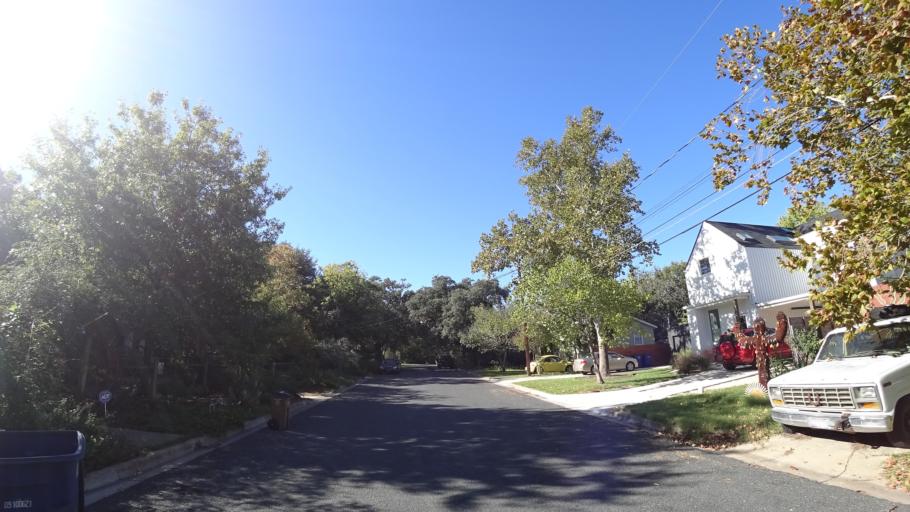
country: US
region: Texas
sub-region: Travis County
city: Austin
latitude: 30.2367
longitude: -97.7609
